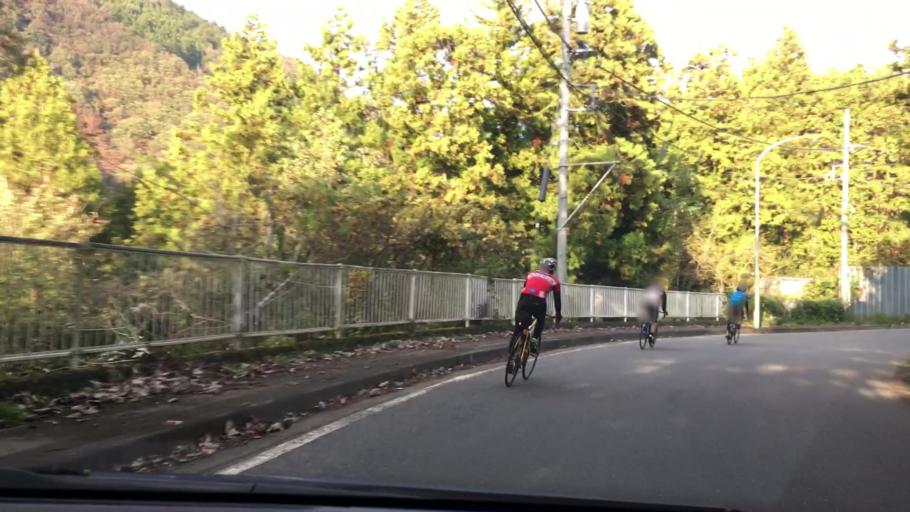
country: JP
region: Yamanashi
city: Uenohara
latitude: 35.5481
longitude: 139.1322
